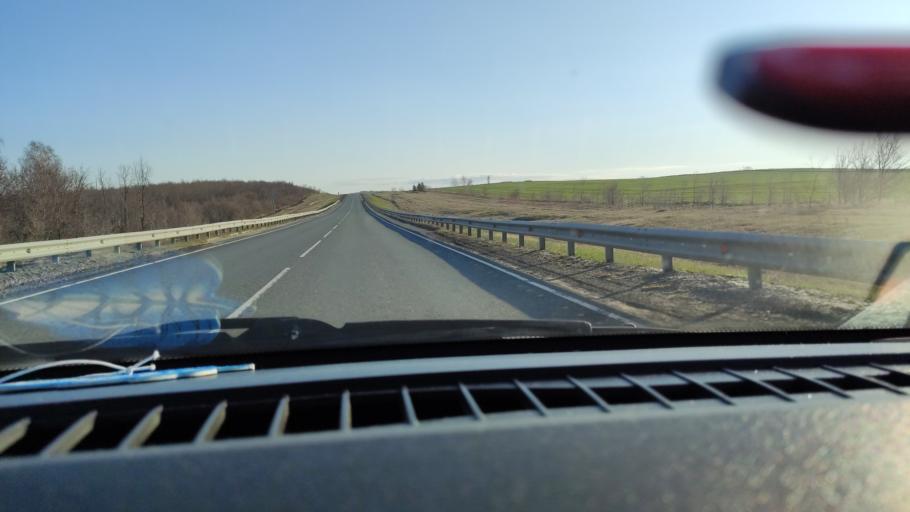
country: RU
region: Saratov
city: Balakovo
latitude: 52.1891
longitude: 47.8512
